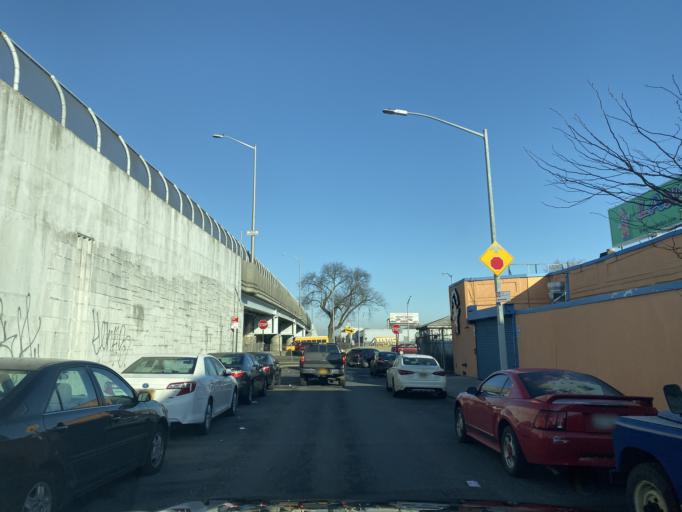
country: US
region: New York
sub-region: Kings County
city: Coney Island
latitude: 40.5840
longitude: -73.9600
